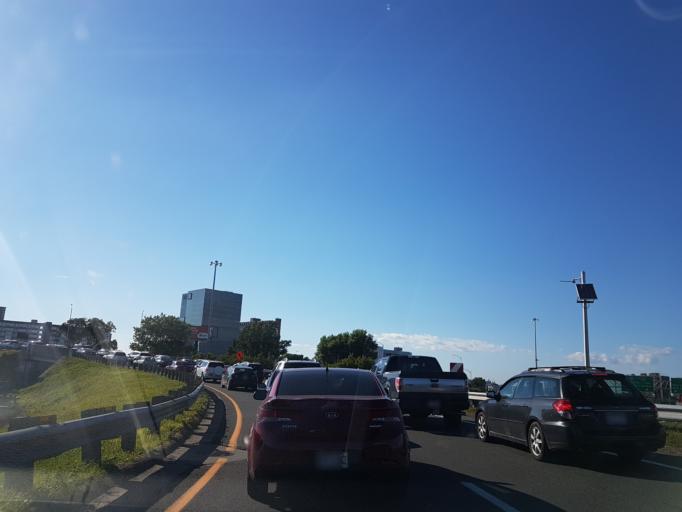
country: CA
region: Quebec
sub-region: Monteregie
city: Longueuil
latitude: 45.5228
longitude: -73.5149
